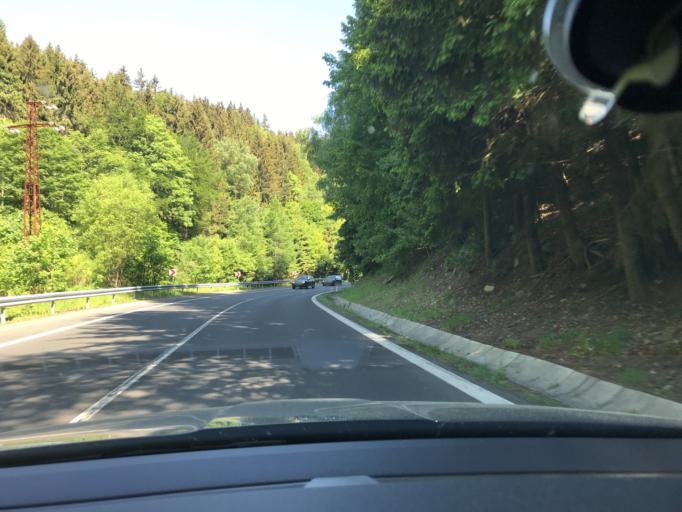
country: CZ
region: Karlovarsky
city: Jachymov
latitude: 50.3501
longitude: 12.9324
